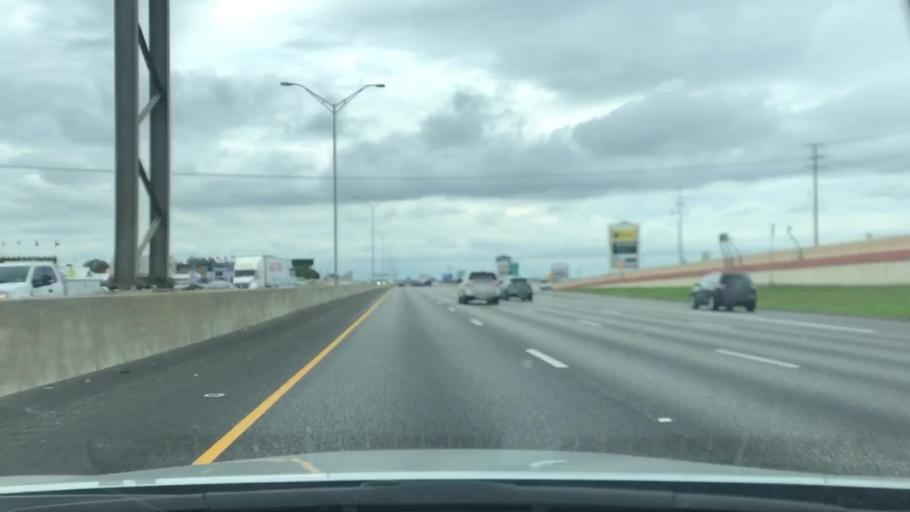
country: US
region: Texas
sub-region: Comal County
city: New Braunfels
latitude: 29.6837
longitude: -98.1373
